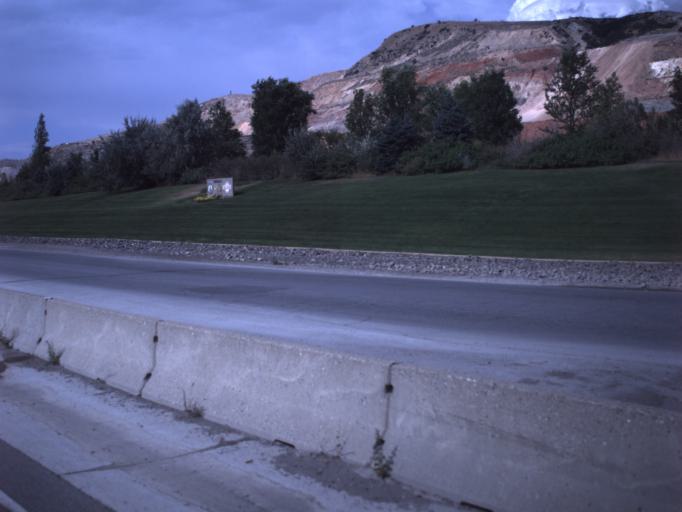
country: US
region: Utah
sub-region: Davis County
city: North Salt Lake
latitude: 40.8080
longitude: -111.9183
